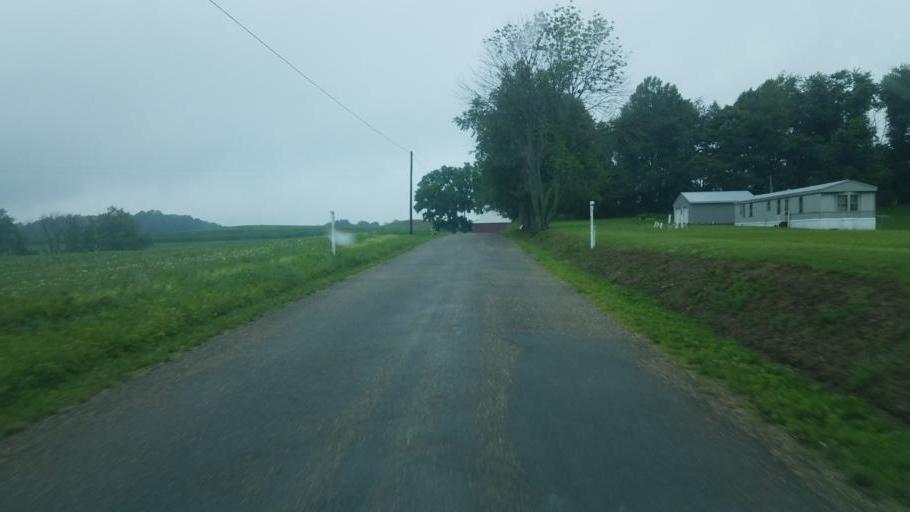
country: US
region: Ohio
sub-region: Carroll County
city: Carrollton
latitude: 40.4514
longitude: -81.0998
